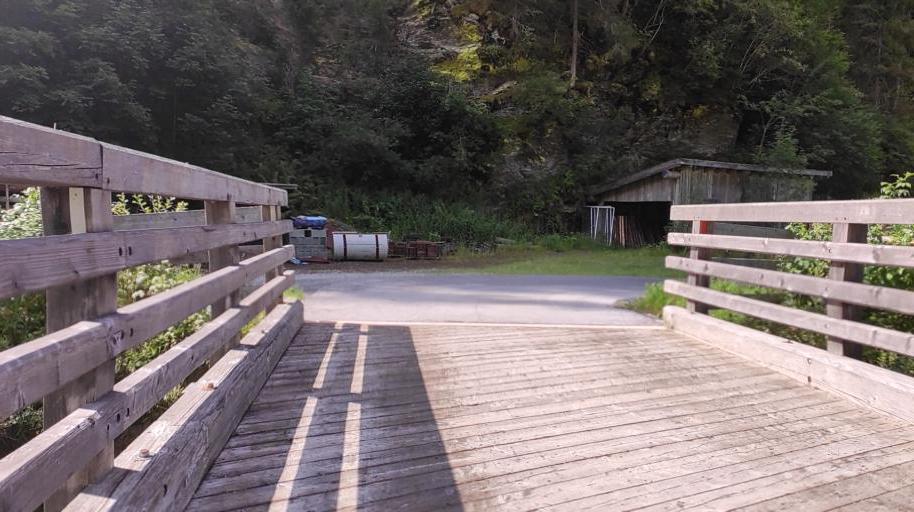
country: AT
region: Salzburg
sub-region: Politischer Bezirk Zell am See
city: Viehhofen
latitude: 47.3637
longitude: 12.7594
